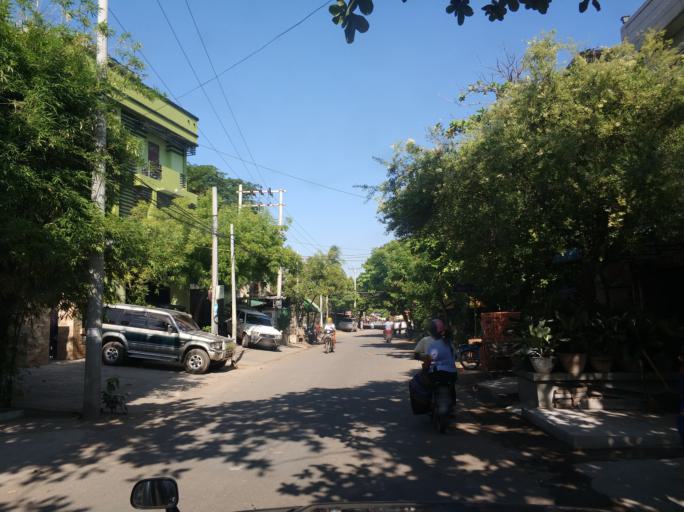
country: MM
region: Mandalay
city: Mandalay
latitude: 21.9718
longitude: 96.0710
